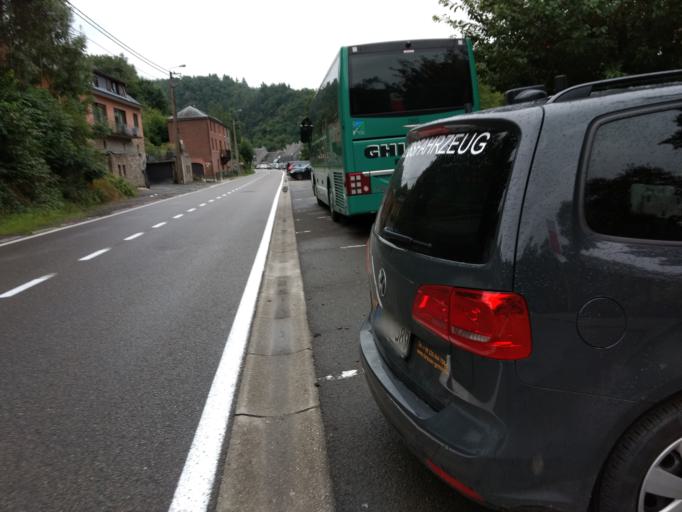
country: BE
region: Wallonia
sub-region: Province du Luxembourg
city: La Roche-en-Ardenne
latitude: 50.1798
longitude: 5.5838
